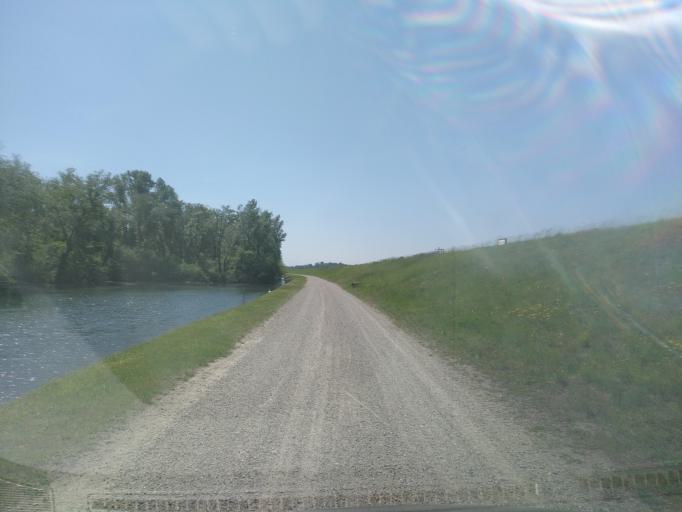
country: FR
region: Alsace
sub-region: Departement du Haut-Rhin
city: Kunheim
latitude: 48.0831
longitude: 7.5714
